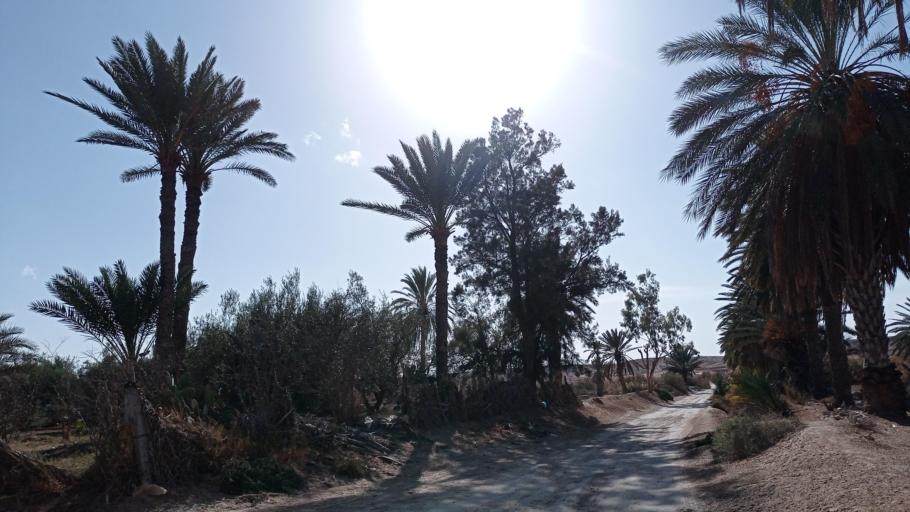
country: TN
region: Qabis
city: Gabes
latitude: 33.8294
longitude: 10.1121
